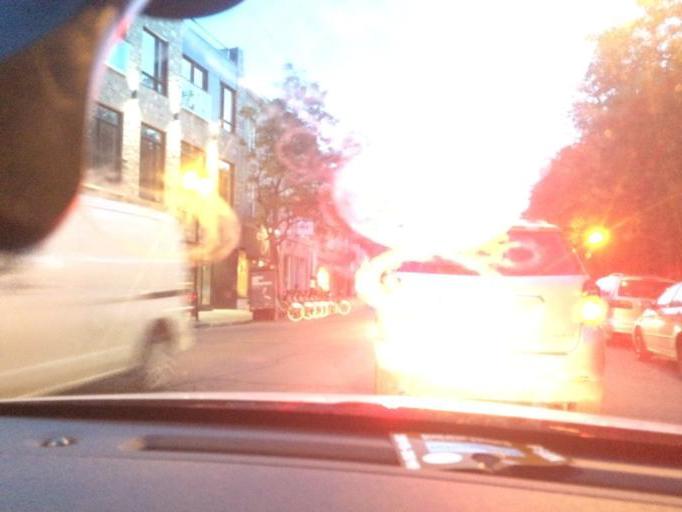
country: CA
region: Quebec
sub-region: Montreal
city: Montreal
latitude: 45.4870
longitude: -73.5694
